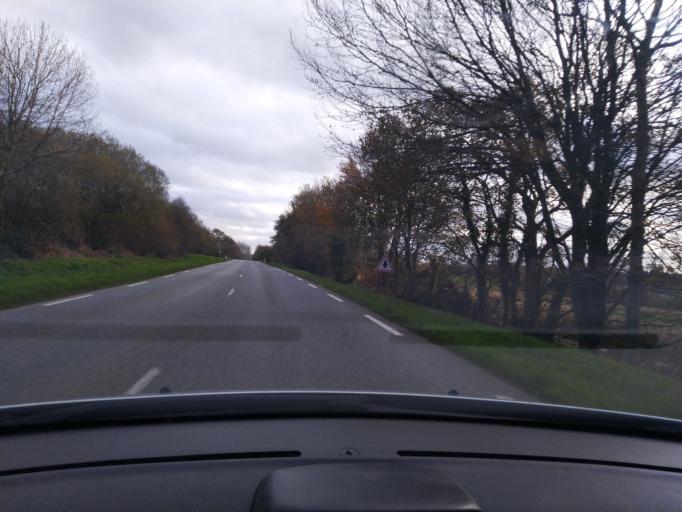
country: FR
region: Brittany
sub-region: Departement des Cotes-d'Armor
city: Plouaret
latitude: 48.5900
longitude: -3.4960
